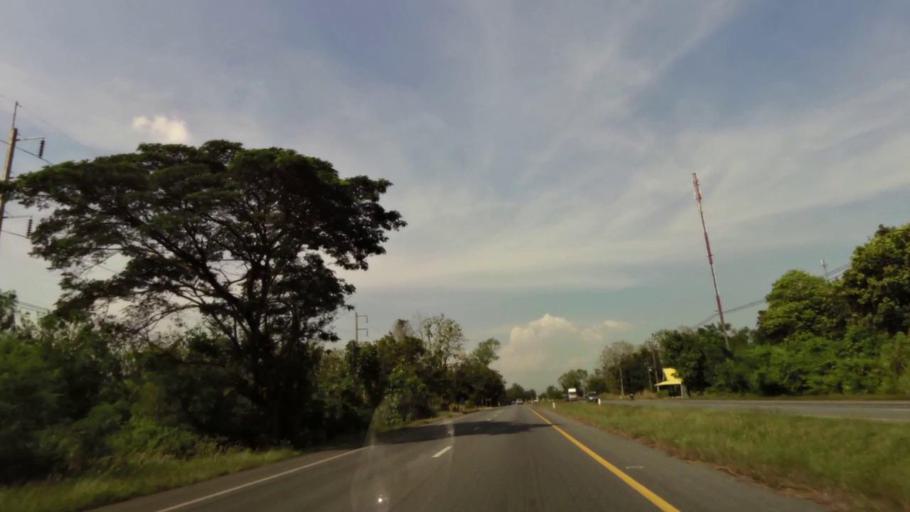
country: TH
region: Uttaradit
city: Tron
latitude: 17.5563
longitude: 100.1699
